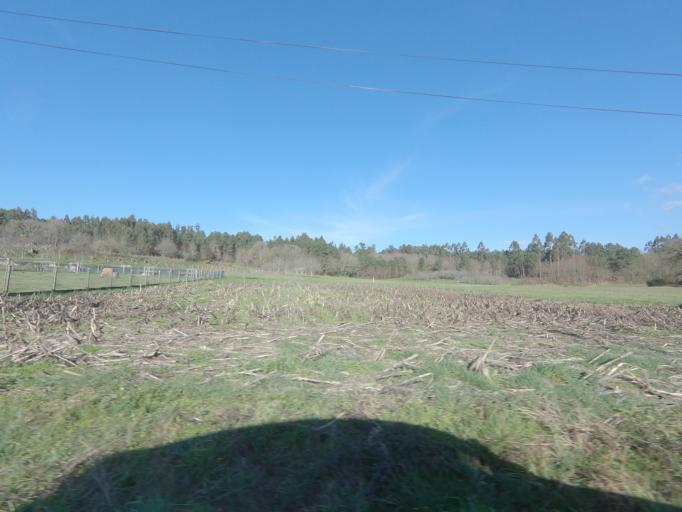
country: ES
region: Galicia
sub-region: Provincia da Coruna
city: Ribeira
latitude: 42.7141
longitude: -8.4352
